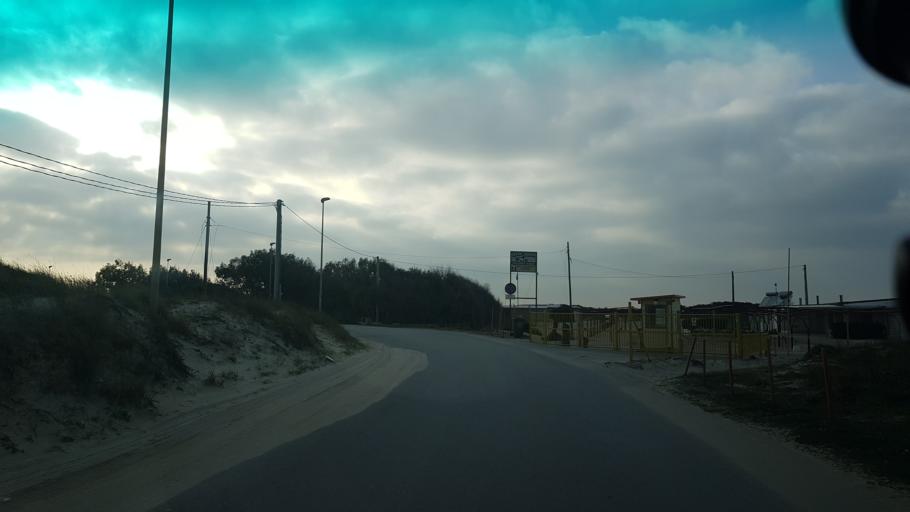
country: IT
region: Apulia
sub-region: Provincia di Brindisi
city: Carovigno
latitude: 40.7448
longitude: 17.7313
